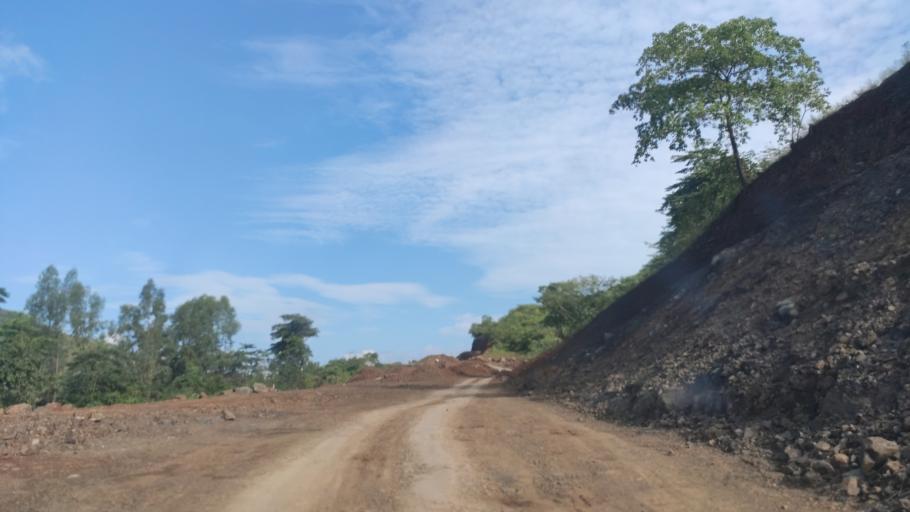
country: ET
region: Southern Nations, Nationalities, and People's Region
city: Arba Minch'
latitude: 6.4251
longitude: 37.3441
